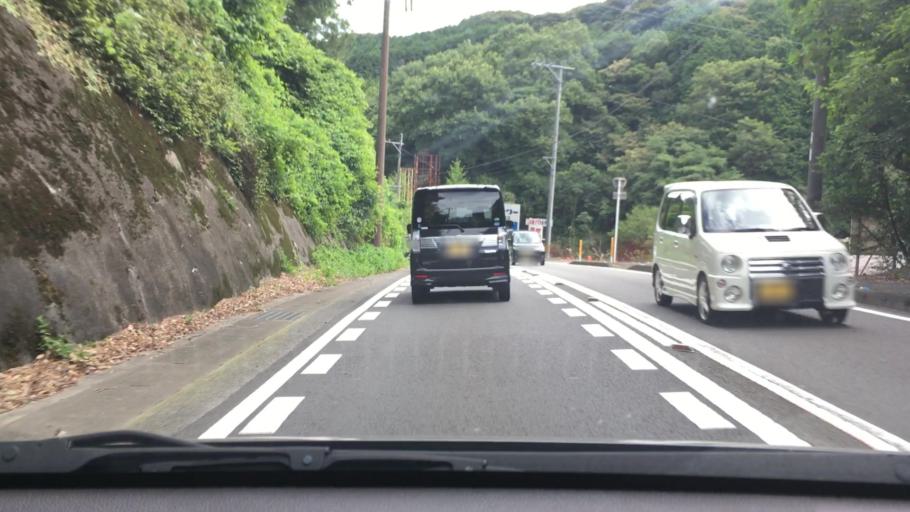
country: JP
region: Nagasaki
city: Togitsu
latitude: 32.9296
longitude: 129.7826
